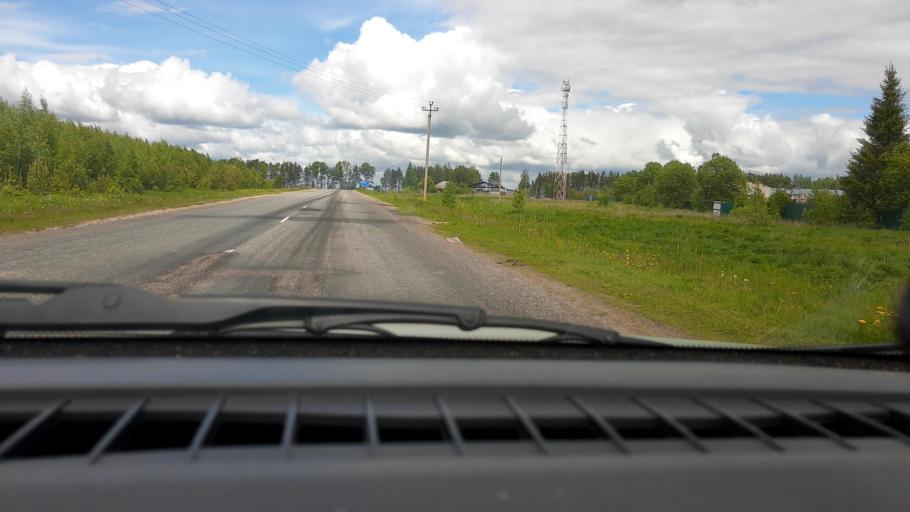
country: RU
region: Nizjnij Novgorod
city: Tonkino
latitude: 57.3684
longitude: 46.4220
